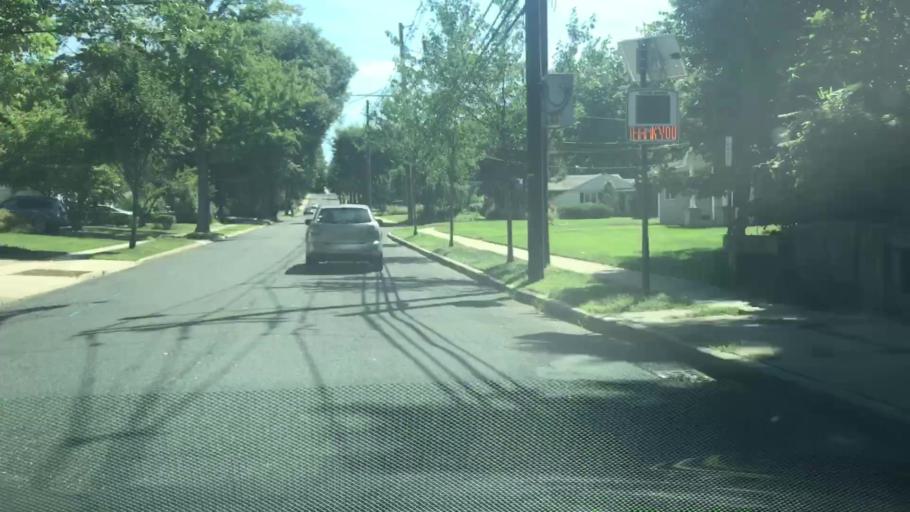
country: US
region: New Jersey
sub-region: Bergen County
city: River Edge
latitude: 40.9206
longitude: -74.0426
